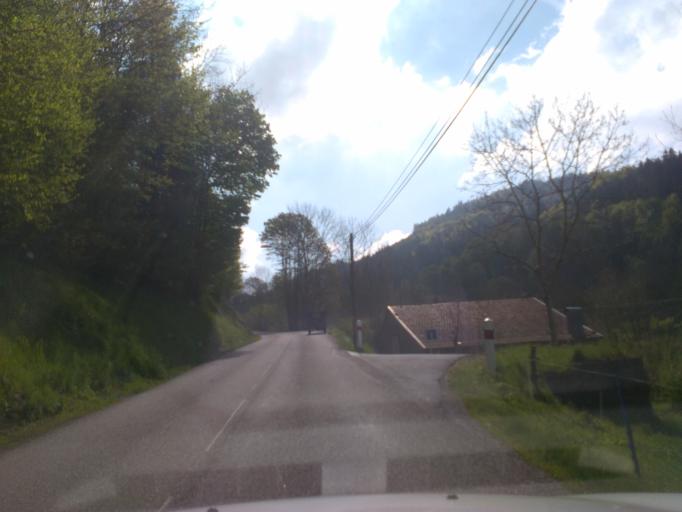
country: FR
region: Lorraine
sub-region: Departement des Vosges
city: Saulxures-sur-Moselotte
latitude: 47.9886
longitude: 6.7770
